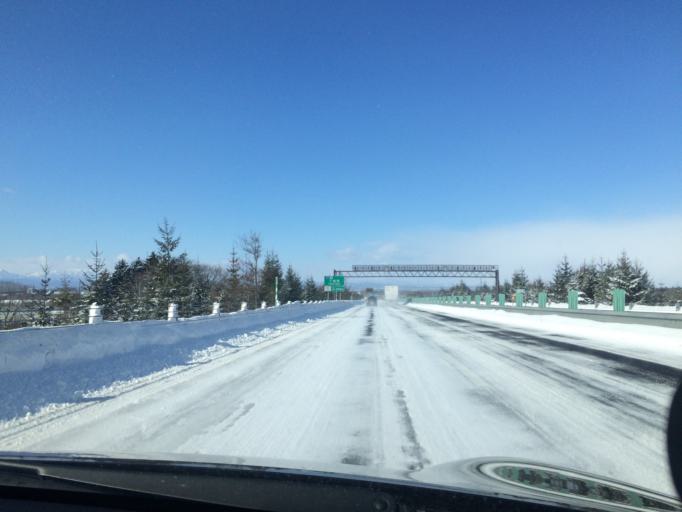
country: JP
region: Hokkaido
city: Chitose
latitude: 42.8796
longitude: 141.7216
